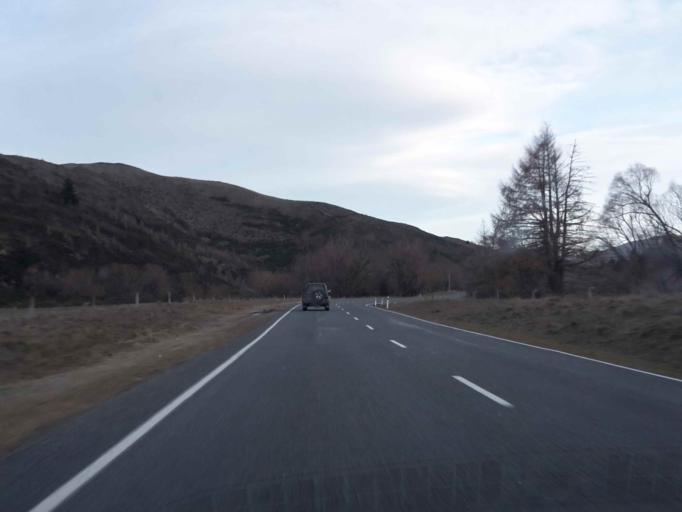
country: NZ
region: Canterbury
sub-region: Timaru District
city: Pleasant Point
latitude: -44.0730
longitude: 170.6666
